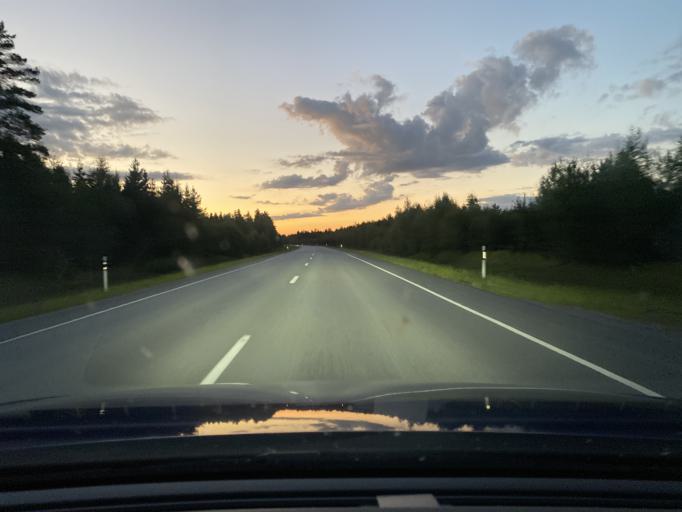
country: FI
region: Varsinais-Suomi
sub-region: Loimaa
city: Oripaeae
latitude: 60.8917
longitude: 22.7021
